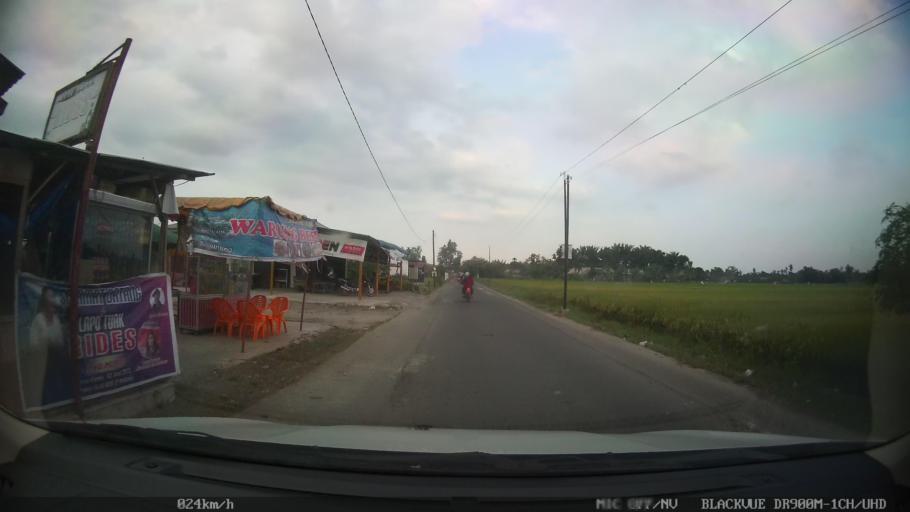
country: ID
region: North Sumatra
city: Sunggal
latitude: 3.5612
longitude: 98.5913
